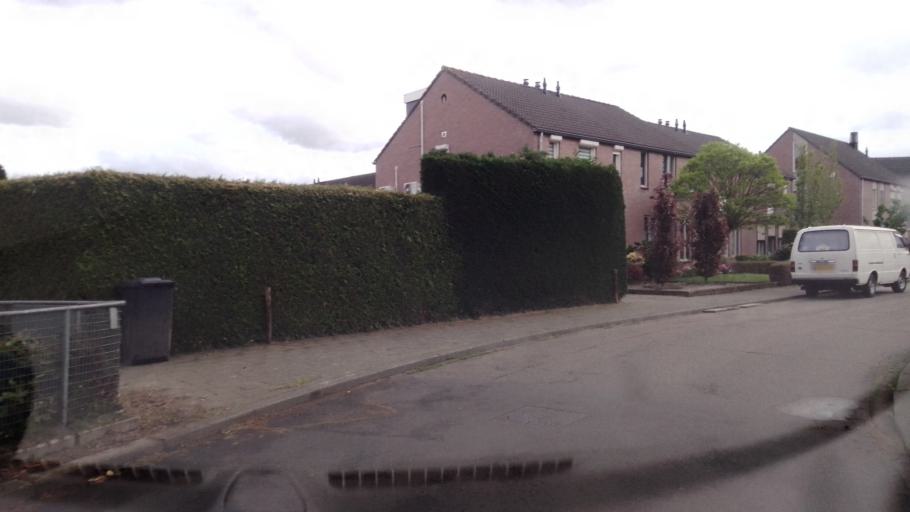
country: NL
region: Limburg
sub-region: Gemeente Venlo
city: Arcen
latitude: 51.4590
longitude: 6.1584
